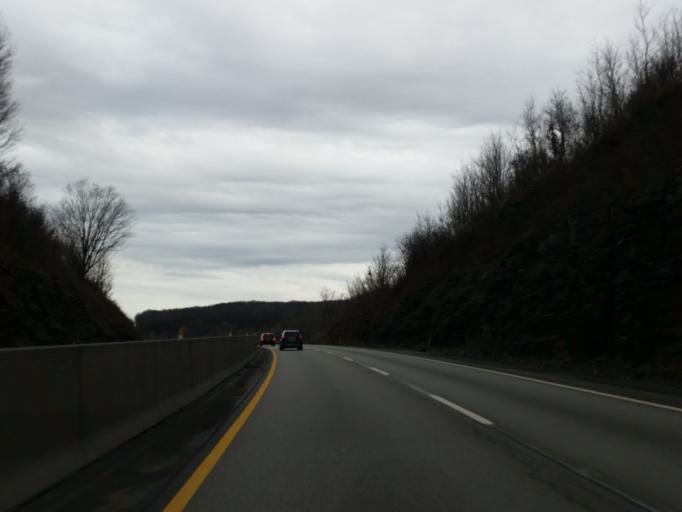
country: US
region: Pennsylvania
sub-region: Somerset County
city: Somerset
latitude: 40.0688
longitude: -79.1566
